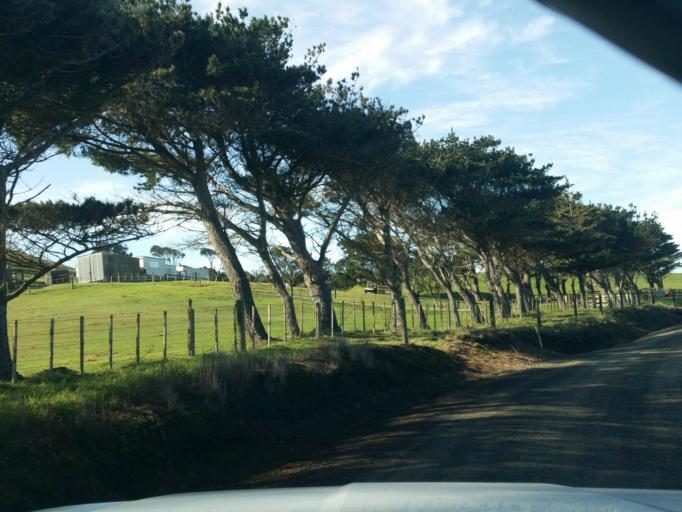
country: NZ
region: Northland
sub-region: Kaipara District
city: Dargaville
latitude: -35.9131
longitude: 173.7222
